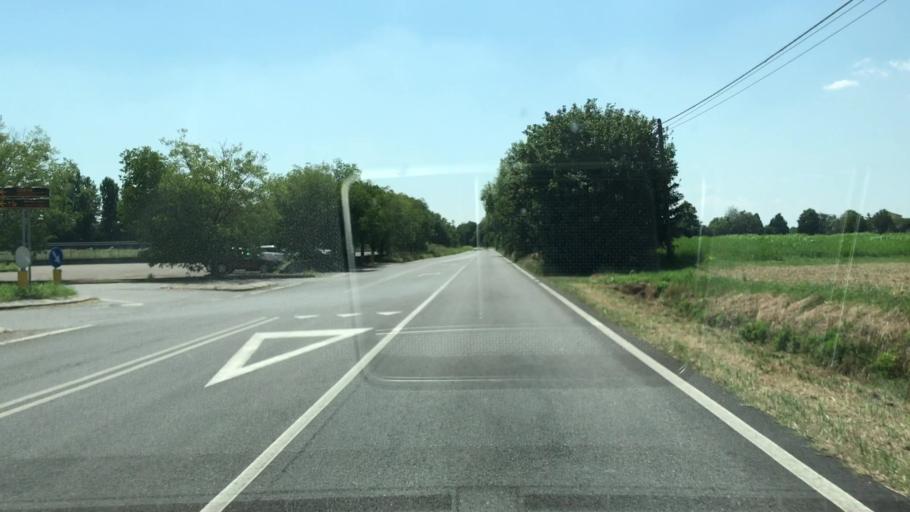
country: IT
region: Lombardy
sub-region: Provincia di Mantova
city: Pegognaga
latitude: 44.9987
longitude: 10.8846
